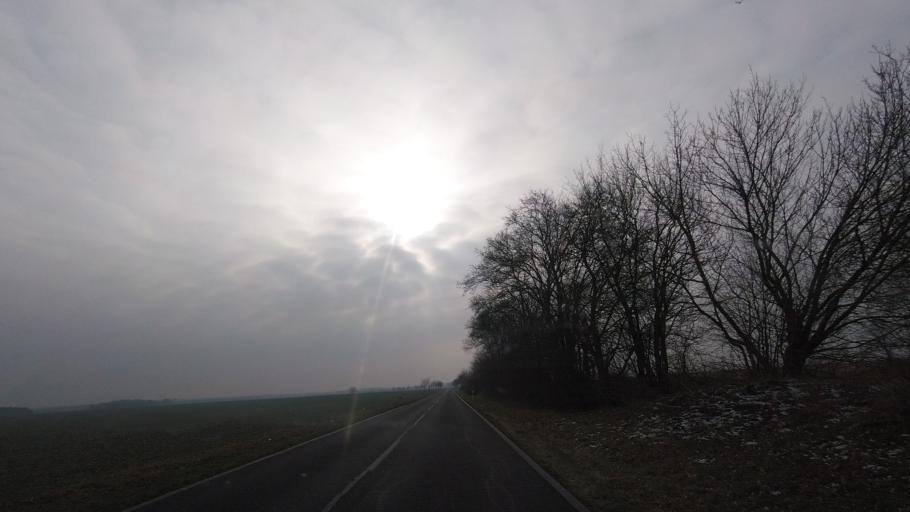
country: DE
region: Brandenburg
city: Juterbog
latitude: 51.9732
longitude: 13.0739
